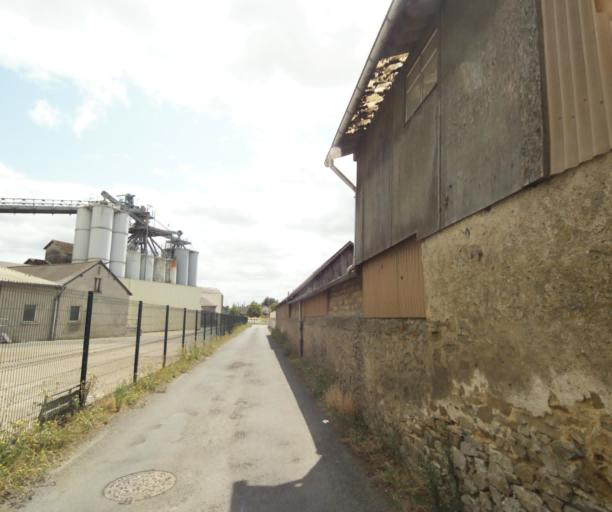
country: FR
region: Pays de la Loire
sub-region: Departement de la Sarthe
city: Sable-sur-Sarthe
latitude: 47.8431
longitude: -0.3429
